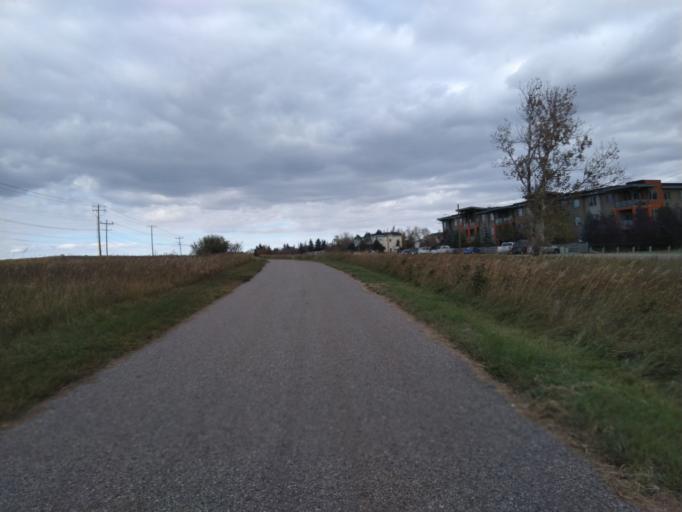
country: CA
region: Alberta
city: Calgary
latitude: 51.0275
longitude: -113.9962
